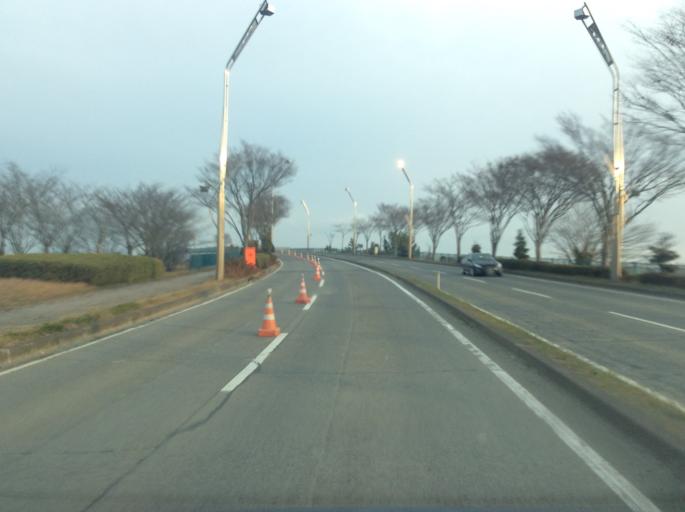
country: JP
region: Miyagi
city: Iwanuma
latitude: 38.1347
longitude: 140.9010
